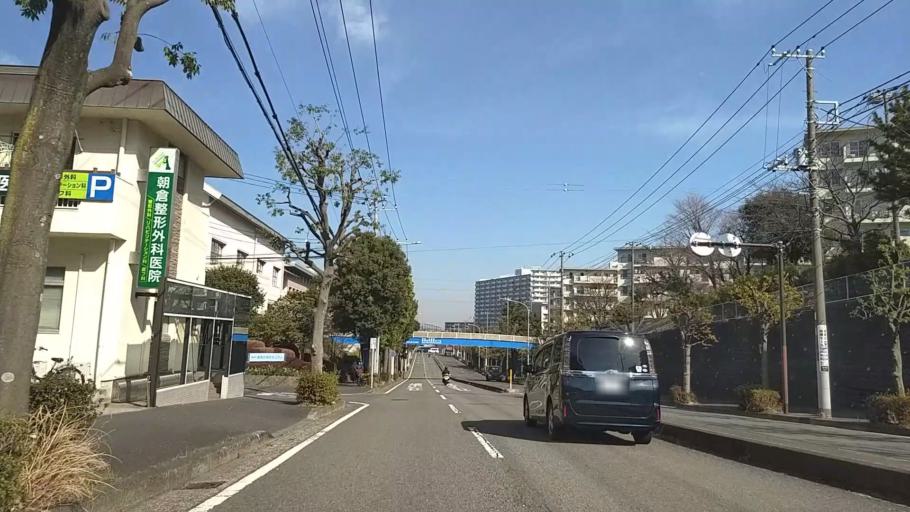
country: JP
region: Kanagawa
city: Kamakura
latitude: 35.3706
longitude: 139.5828
